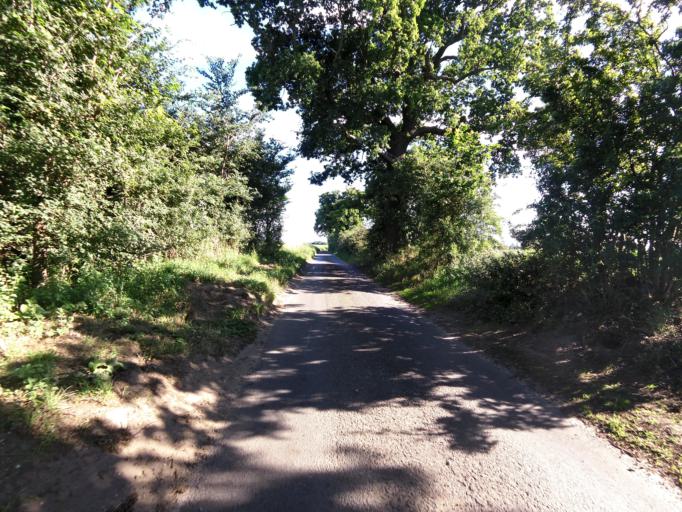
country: GB
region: England
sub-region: Suffolk
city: Kesgrave
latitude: 52.0390
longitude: 1.2543
